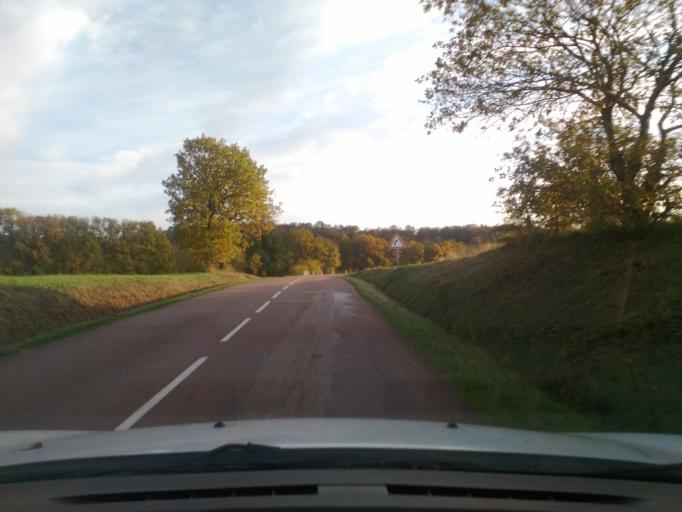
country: FR
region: Lorraine
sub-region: Departement des Vosges
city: Mirecourt
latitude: 48.2198
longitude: 6.1559
